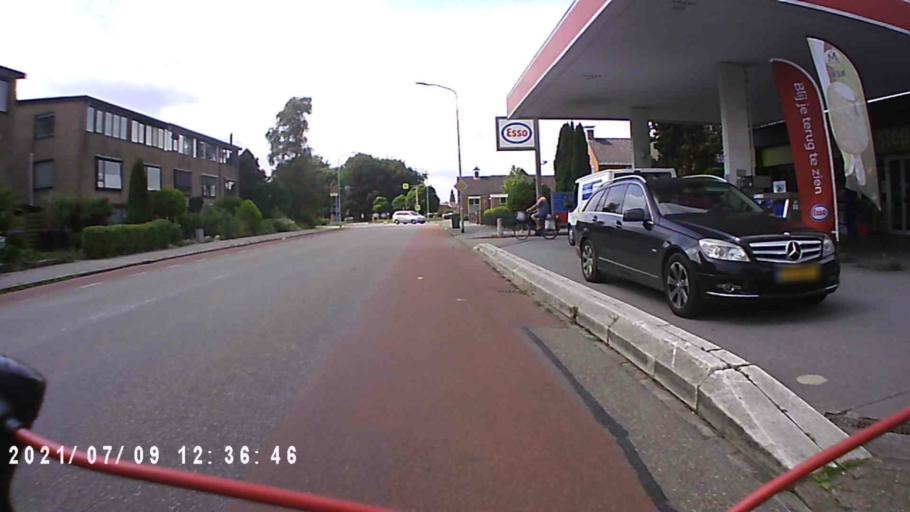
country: NL
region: Groningen
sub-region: Gemeente  Oldambt
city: Winschoten
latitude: 53.1472
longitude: 7.0241
